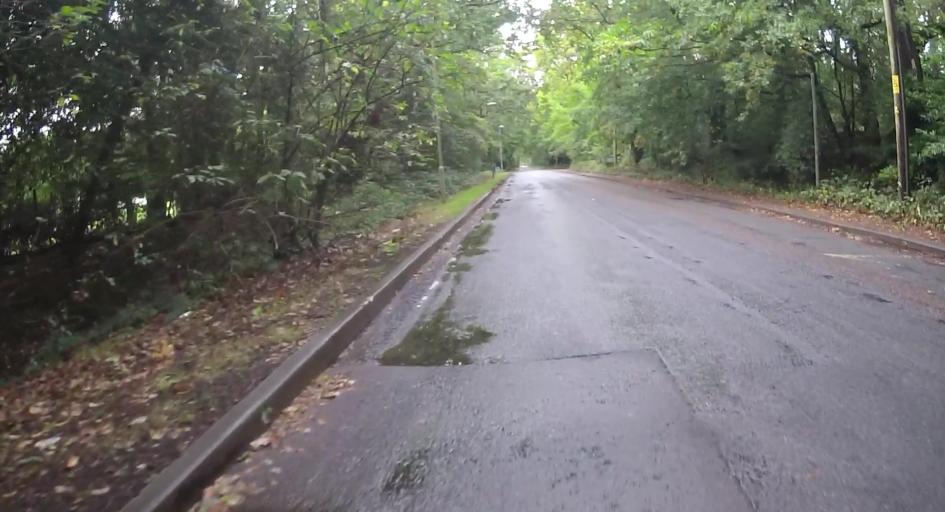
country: GB
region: England
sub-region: Hampshire
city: Tadley
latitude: 51.3570
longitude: -1.1750
